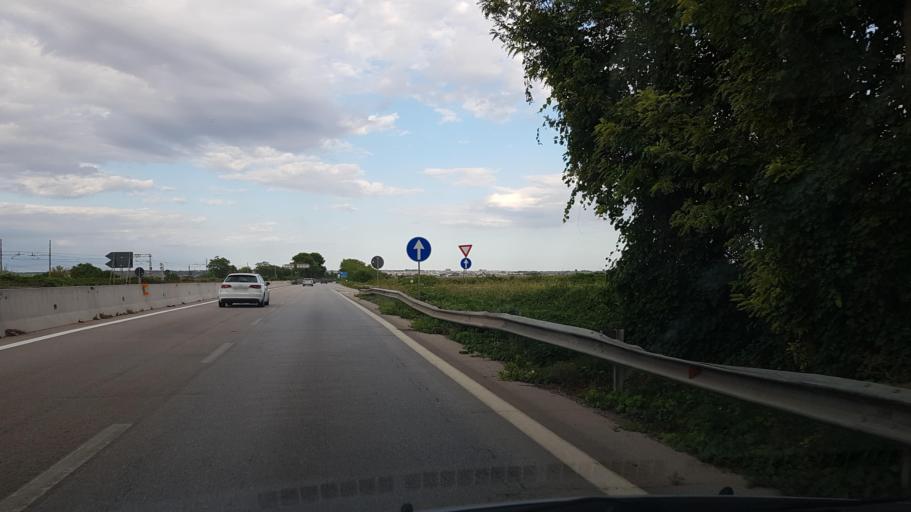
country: IT
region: Apulia
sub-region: Provincia di Taranto
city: Monteiasi
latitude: 40.5240
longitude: 17.3661
